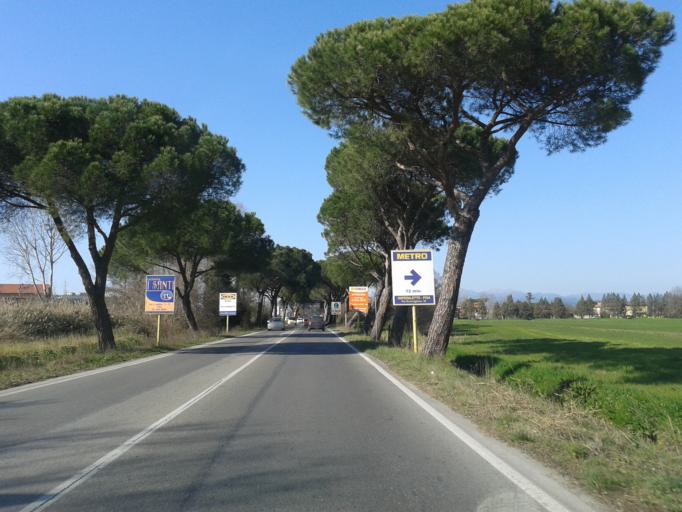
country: IT
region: Tuscany
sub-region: Province of Pisa
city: Madonna dell'Acqua
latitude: 43.7203
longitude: 10.3808
